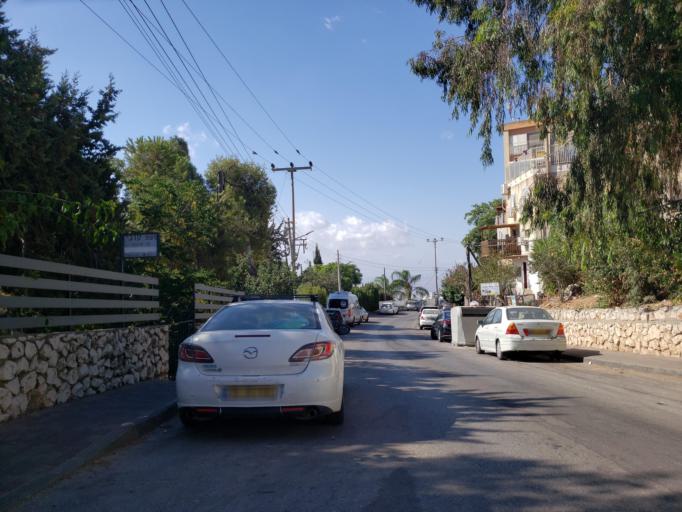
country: IL
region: Northern District
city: Safed
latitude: 32.9575
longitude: 35.5005
